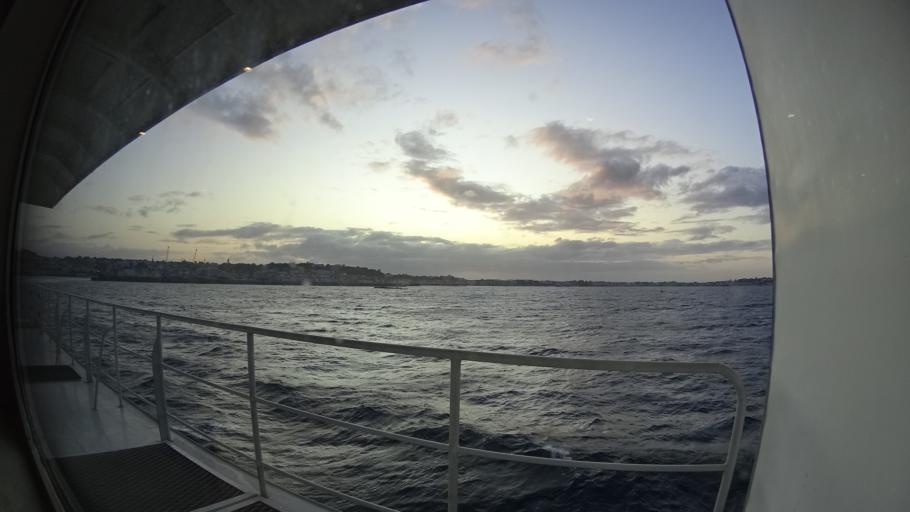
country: GG
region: St Peter Port
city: Saint Peter Port
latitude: 49.4581
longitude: -2.5175
